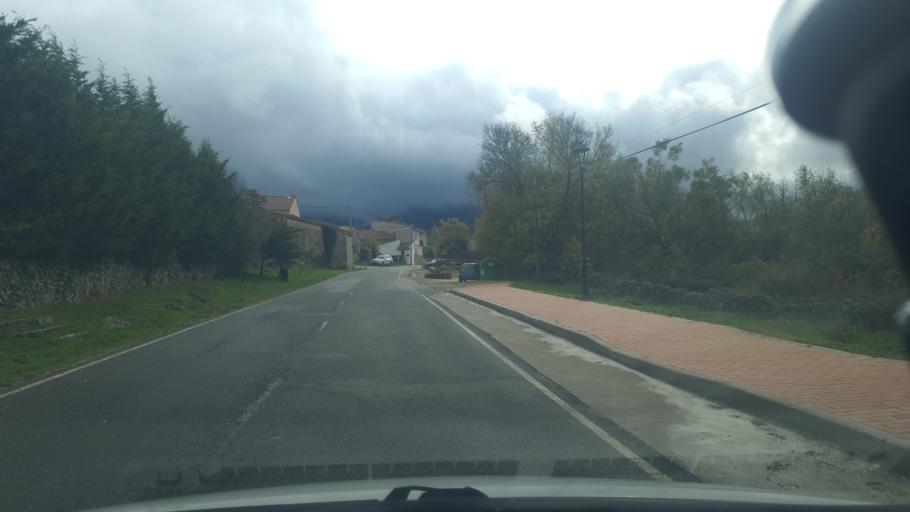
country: ES
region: Castille and Leon
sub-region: Provincia de Segovia
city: Gallegos
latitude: 41.0770
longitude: -3.7863
